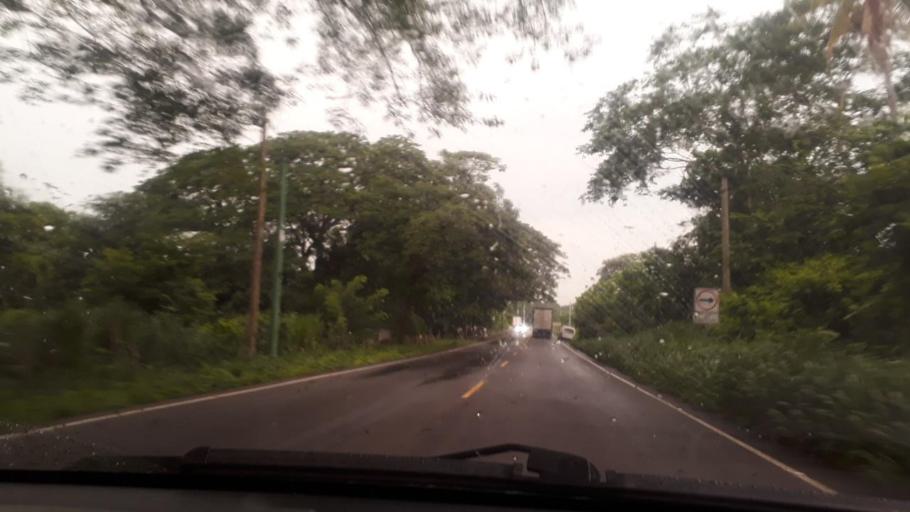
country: GT
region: Santa Rosa
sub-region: Municipio de Taxisco
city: Taxisco
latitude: 14.0937
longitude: -90.5526
